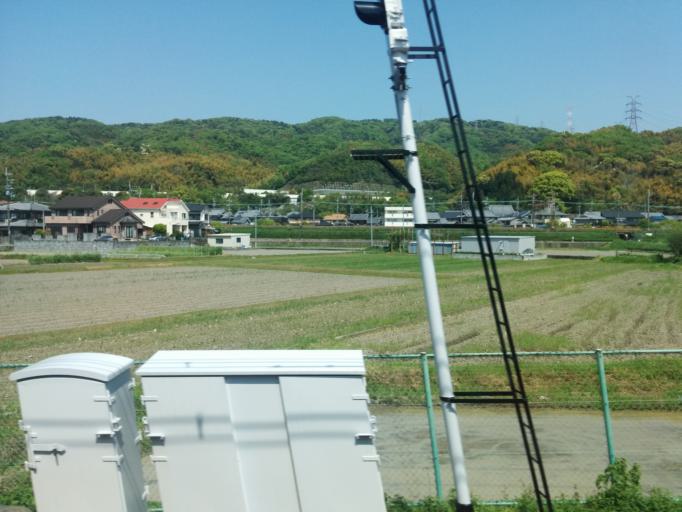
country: JP
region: Osaka
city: Takatsuki
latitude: 34.8637
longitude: 135.6521
